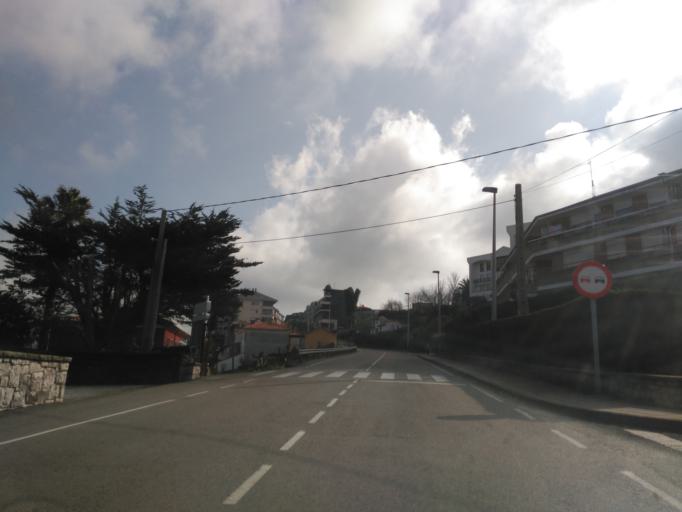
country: ES
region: Cantabria
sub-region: Provincia de Cantabria
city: Suances
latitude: 43.4292
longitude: -4.0445
